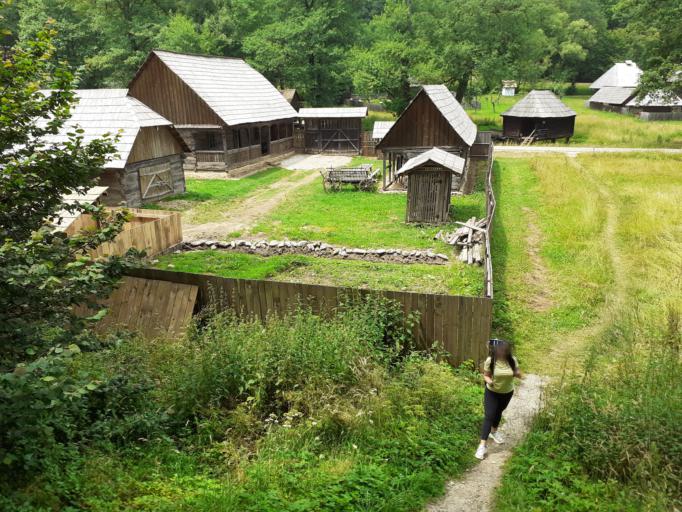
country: RO
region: Sibiu
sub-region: Oras Cisnadie
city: Cisnadie
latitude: 45.7503
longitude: 24.1111
